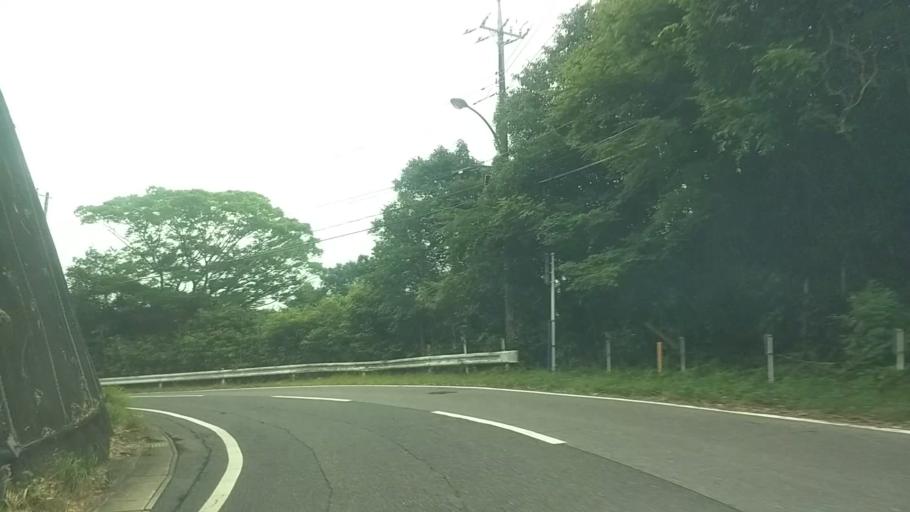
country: JP
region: Chiba
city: Kimitsu
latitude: 35.2312
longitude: 140.0048
